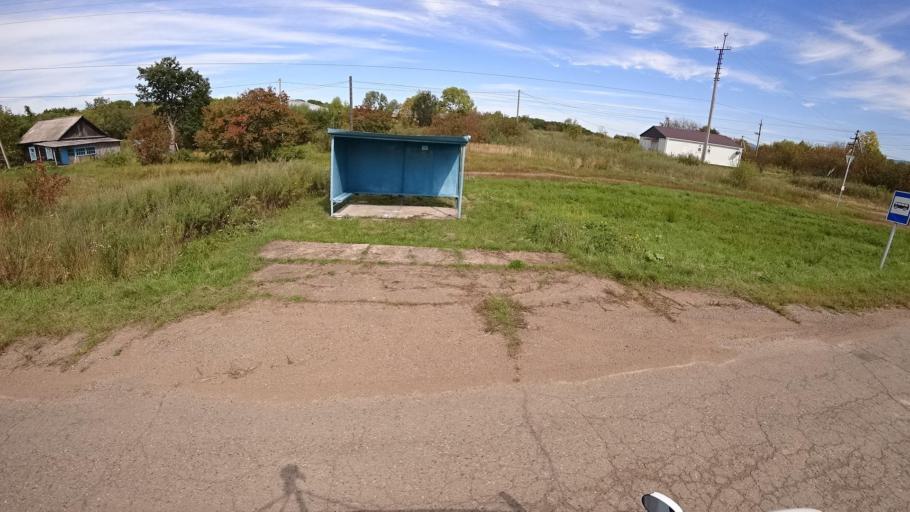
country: RU
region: Primorskiy
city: Yakovlevka
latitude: 44.7099
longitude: 133.6351
